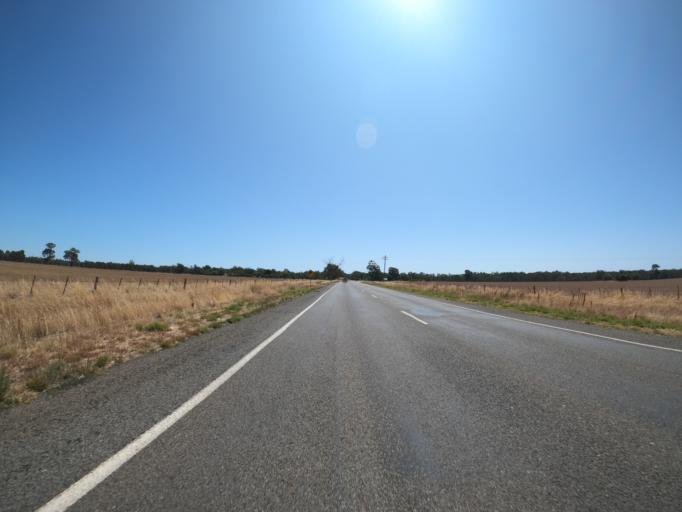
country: AU
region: New South Wales
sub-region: Corowa Shire
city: Corowa
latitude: -36.0706
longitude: 146.2116
